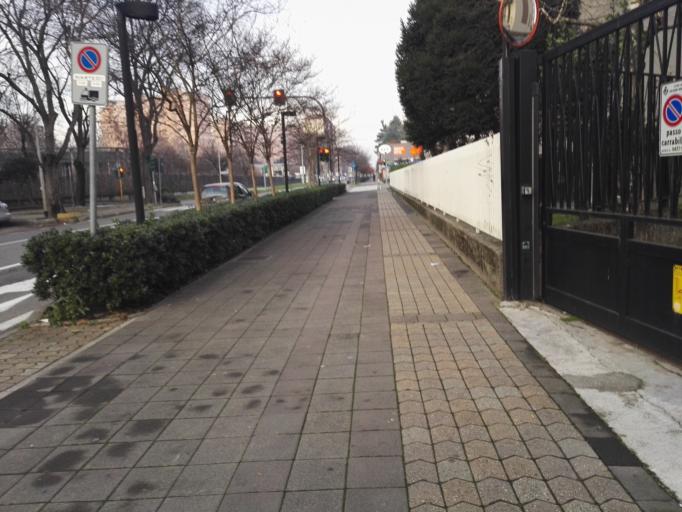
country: IT
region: Lombardy
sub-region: Citta metropolitana di Milano
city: Cologno Monzese
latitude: 45.5317
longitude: 9.2814
